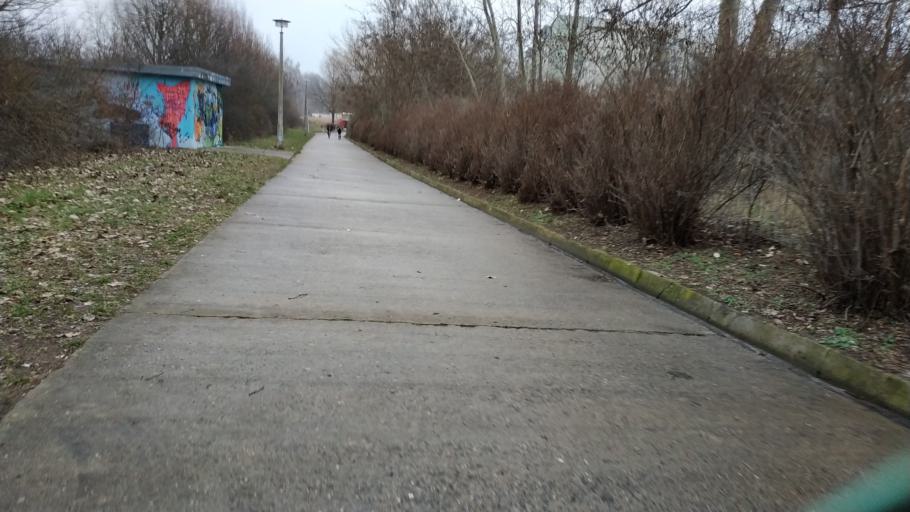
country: DE
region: Berlin
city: Marzahn
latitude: 52.5428
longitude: 13.5843
